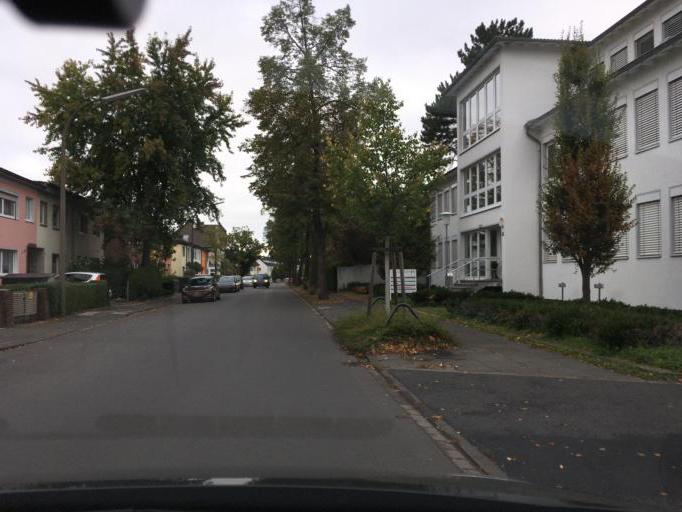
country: DE
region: North Rhine-Westphalia
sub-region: Regierungsbezirk Koln
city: Bonn
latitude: 50.7436
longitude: 7.1330
